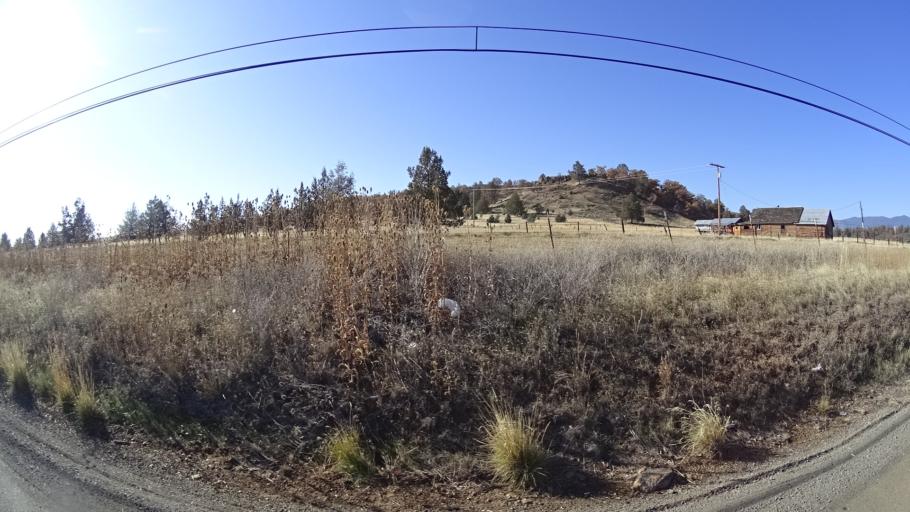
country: US
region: California
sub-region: Siskiyou County
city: Montague
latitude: 41.7087
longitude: -122.5725
